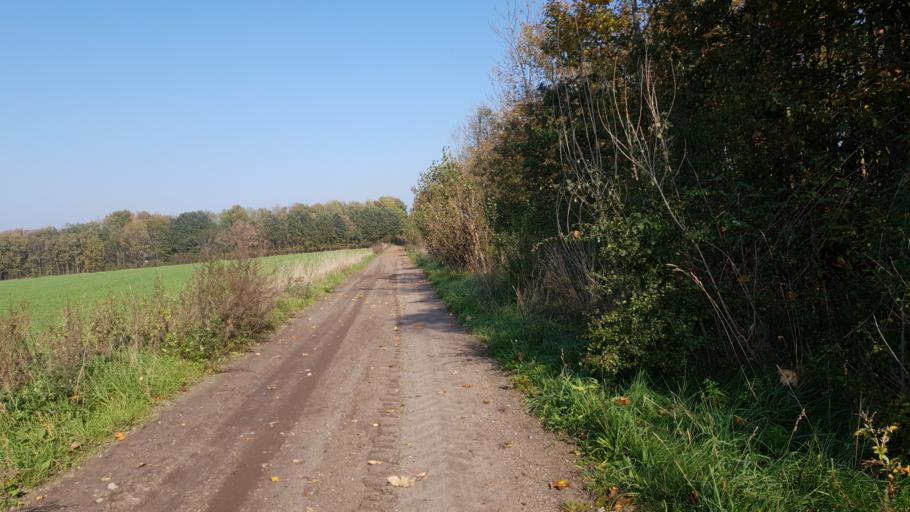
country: DK
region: Central Jutland
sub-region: Hedensted Kommune
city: Hedensted
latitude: 55.7939
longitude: 9.6817
